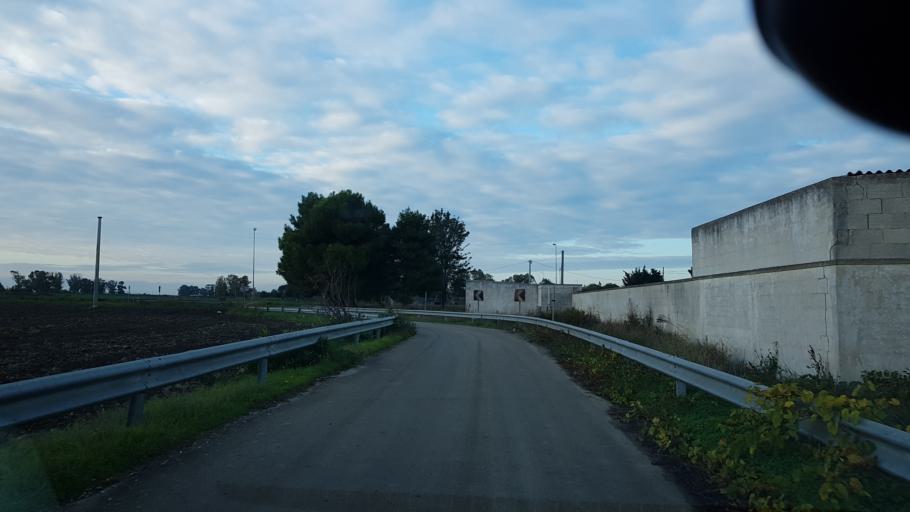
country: IT
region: Apulia
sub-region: Provincia di Brindisi
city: Tuturano
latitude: 40.5653
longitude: 18.0159
